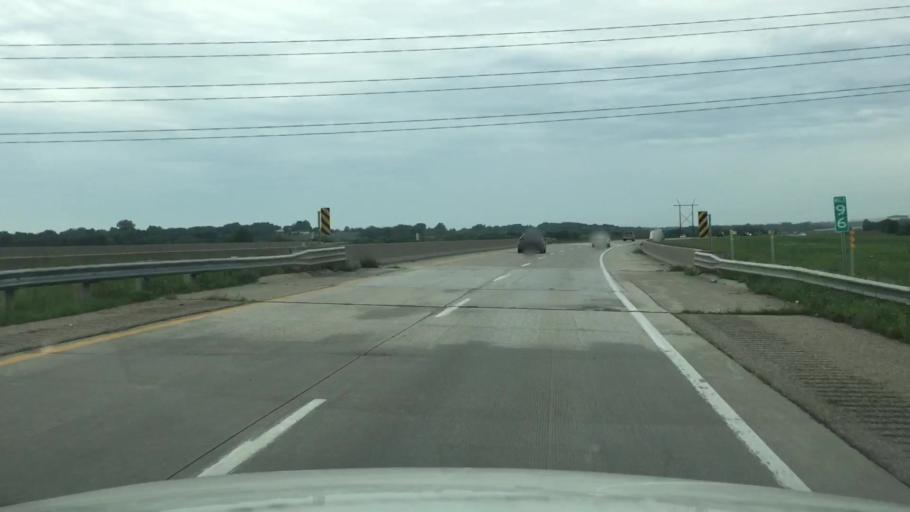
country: US
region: Iowa
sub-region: Warren County
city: Norwalk
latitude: 41.4988
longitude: -93.6250
